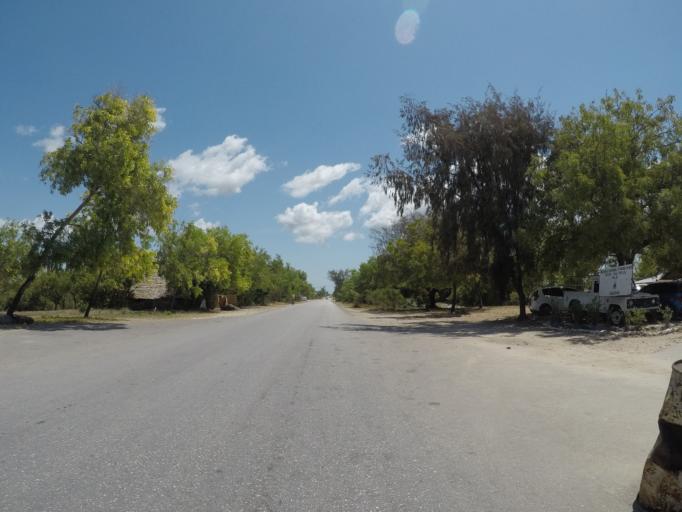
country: TZ
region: Zanzibar Central/South
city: Nganane
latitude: -6.2669
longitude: 39.5286
